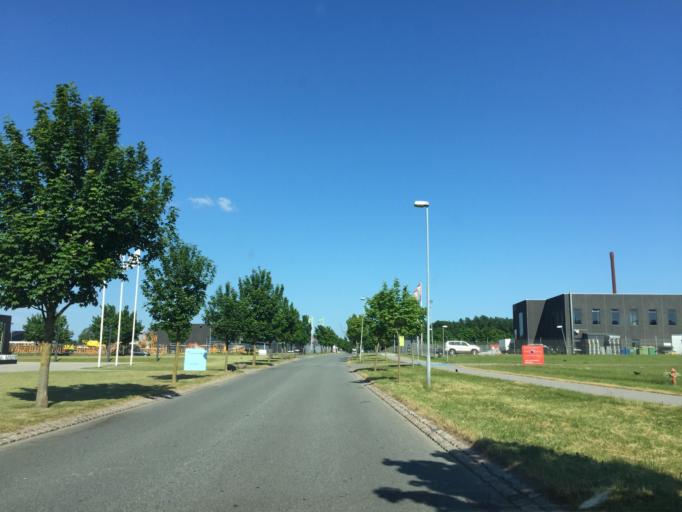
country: DK
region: South Denmark
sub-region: Odense Kommune
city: Hojby
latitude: 55.3451
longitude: 10.3995
